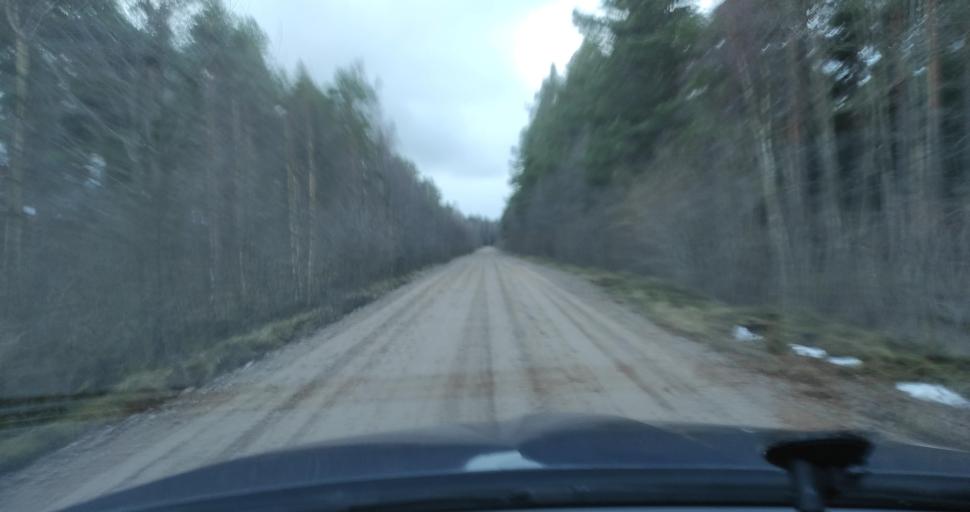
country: LV
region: Pavilostas
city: Pavilosta
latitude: 56.8496
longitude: 21.1085
